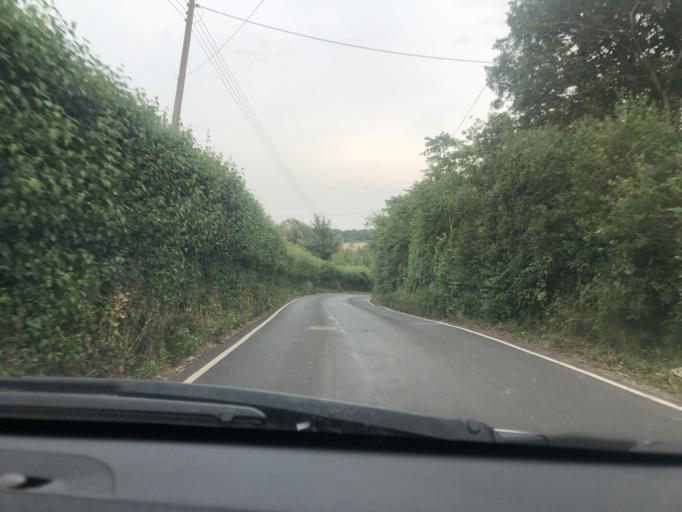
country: GB
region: England
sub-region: Kent
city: Sturry
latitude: 51.3212
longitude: 1.1432
